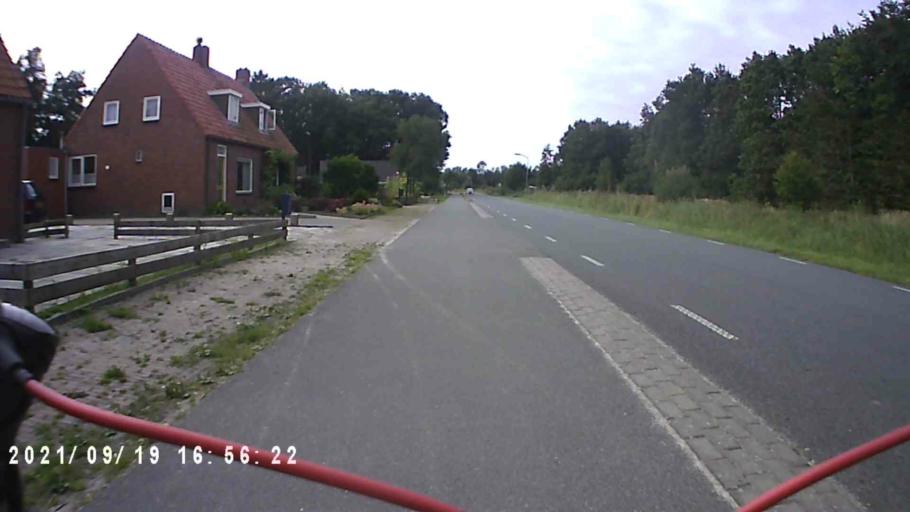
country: NL
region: Groningen
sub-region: Gemeente  Oldambt
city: Winschoten
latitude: 53.1921
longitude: 7.0725
